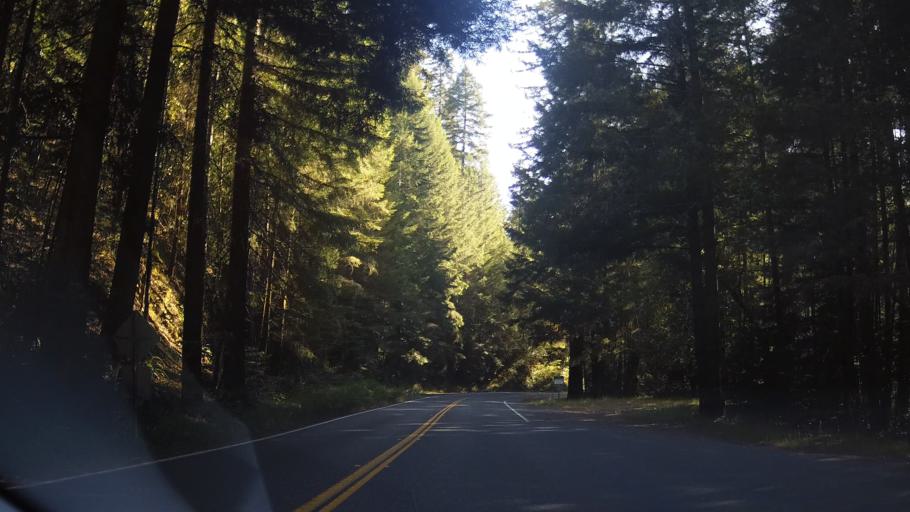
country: US
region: California
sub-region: Mendocino County
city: Brooktrails
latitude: 39.3629
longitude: -123.5038
